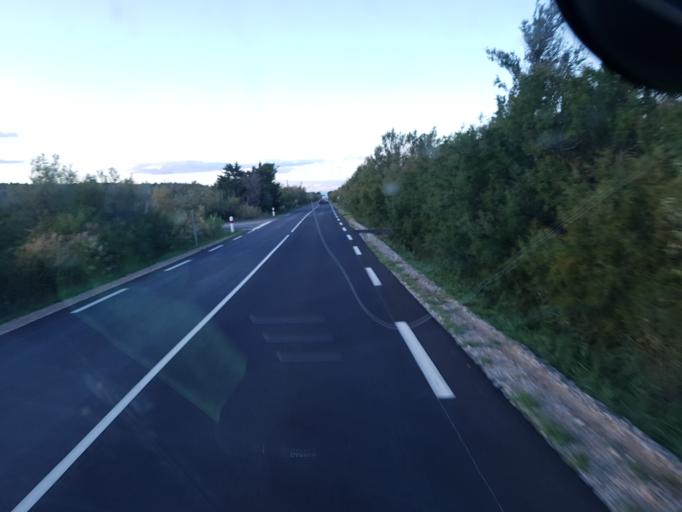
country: FR
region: Languedoc-Roussillon
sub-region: Departement de l'Aude
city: Port-la-Nouvelle
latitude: 42.9982
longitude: 3.0418
